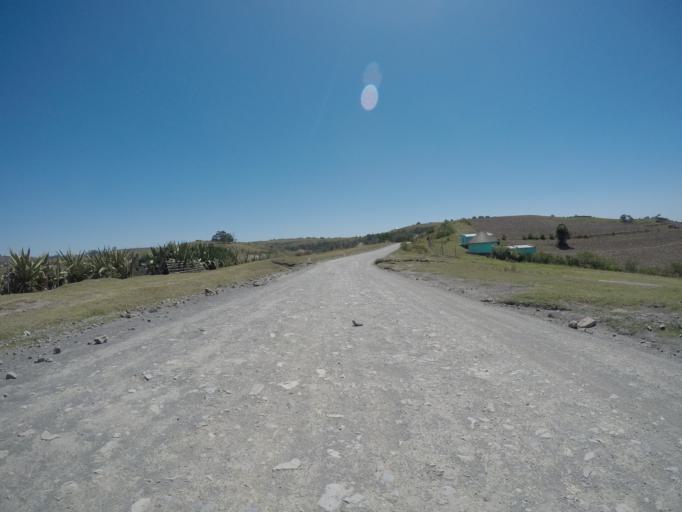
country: ZA
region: Eastern Cape
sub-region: OR Tambo District Municipality
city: Libode
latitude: -31.9924
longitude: 29.0538
